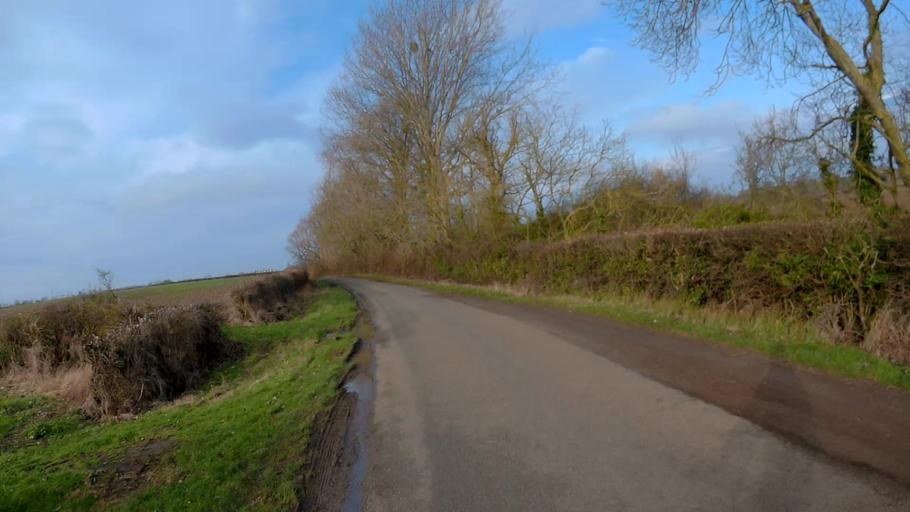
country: GB
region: England
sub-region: Lincolnshire
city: Bourne
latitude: 52.7715
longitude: -0.4246
